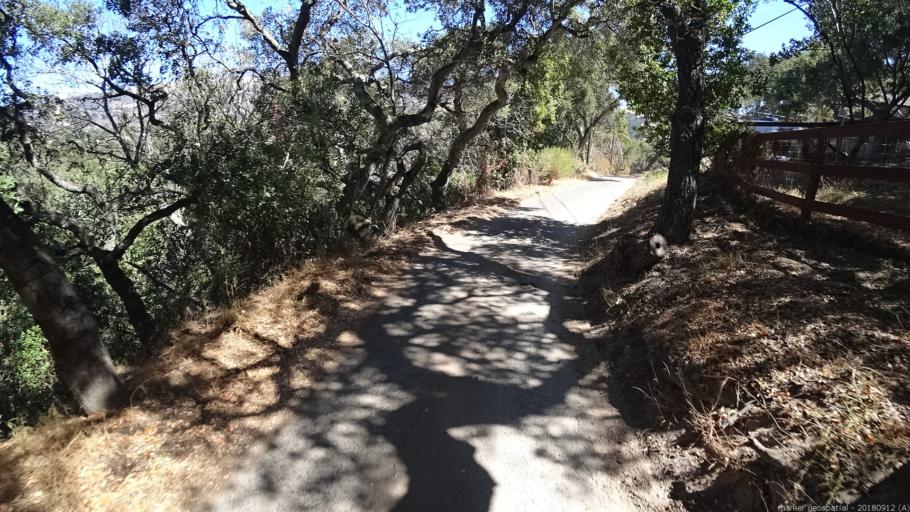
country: US
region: California
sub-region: Monterey County
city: Carmel Valley Village
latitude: 36.4729
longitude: -121.7306
